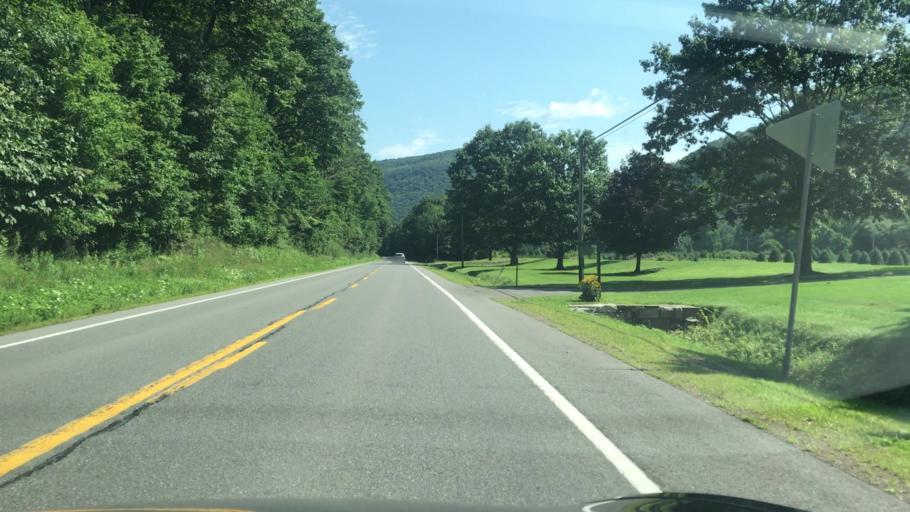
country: US
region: Pennsylvania
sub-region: Bradford County
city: Canton
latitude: 41.4921
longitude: -76.9638
